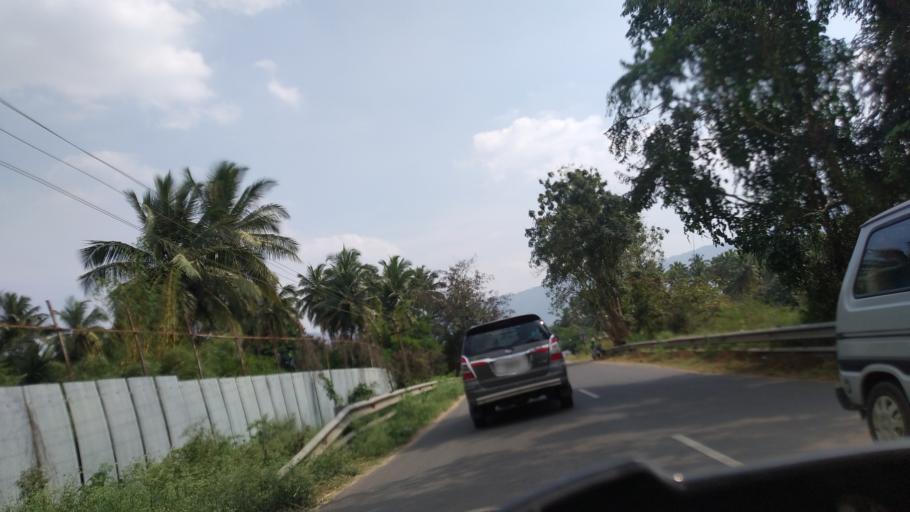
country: IN
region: Tamil Nadu
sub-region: Coimbatore
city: Perur
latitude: 10.9496
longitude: 76.7691
